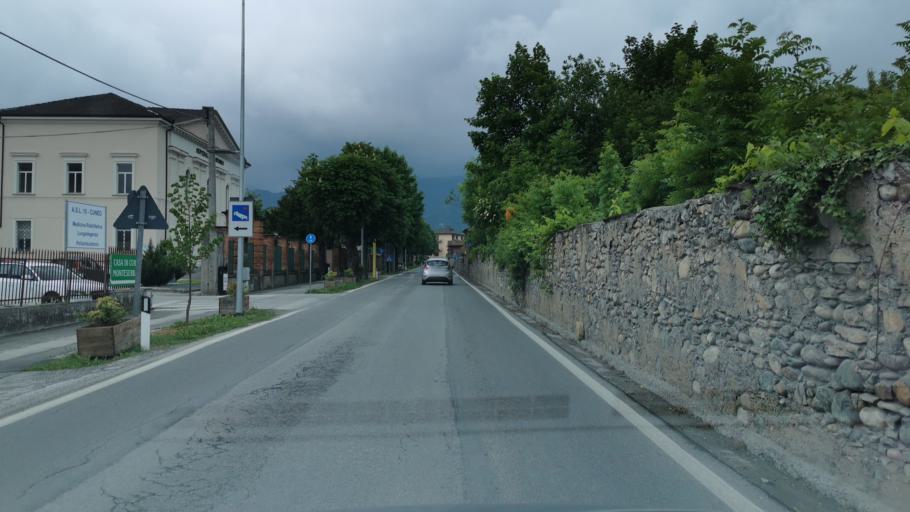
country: IT
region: Piedmont
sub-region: Provincia di Cuneo
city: Caraglio
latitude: 44.4154
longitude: 7.4244
